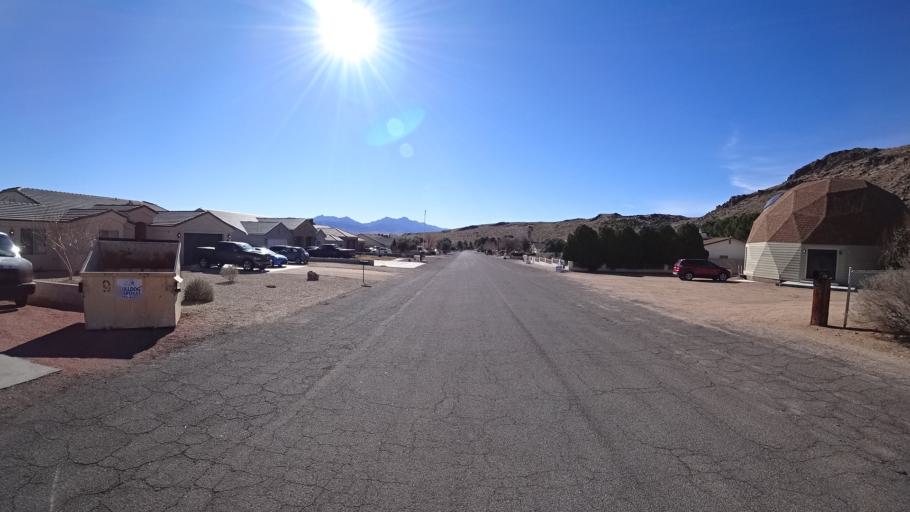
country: US
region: Arizona
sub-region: Mohave County
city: New Kingman-Butler
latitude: 35.2631
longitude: -114.0464
